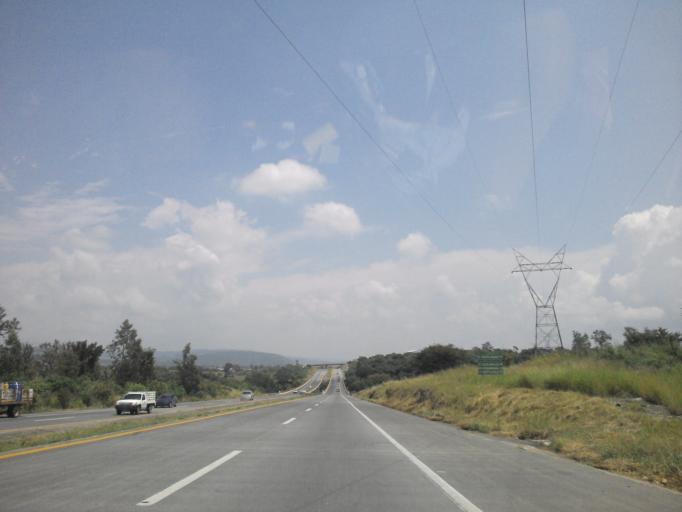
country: MX
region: Jalisco
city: Puente Grande
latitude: 20.5749
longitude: -103.1441
